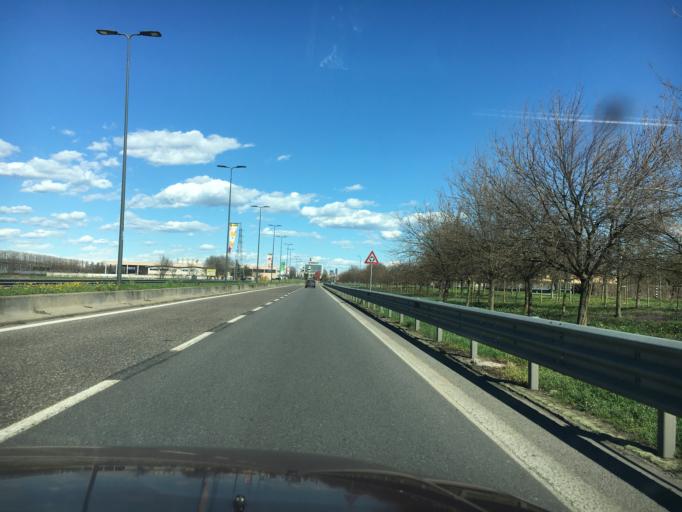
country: IT
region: Lombardy
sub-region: Citta metropolitana di Milano
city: Settimo Milanese
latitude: 45.4558
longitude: 9.0610
